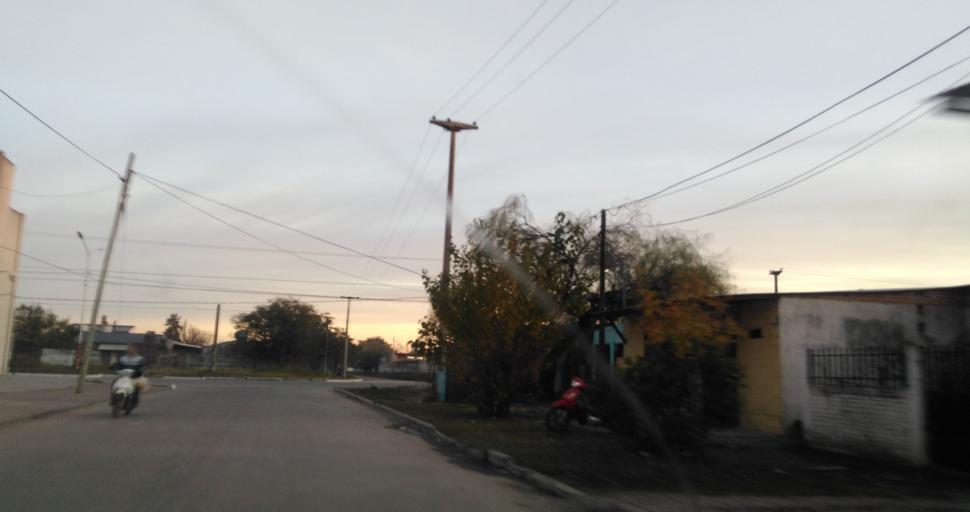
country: AR
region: Chaco
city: Resistencia
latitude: -27.4667
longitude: -59.0028
